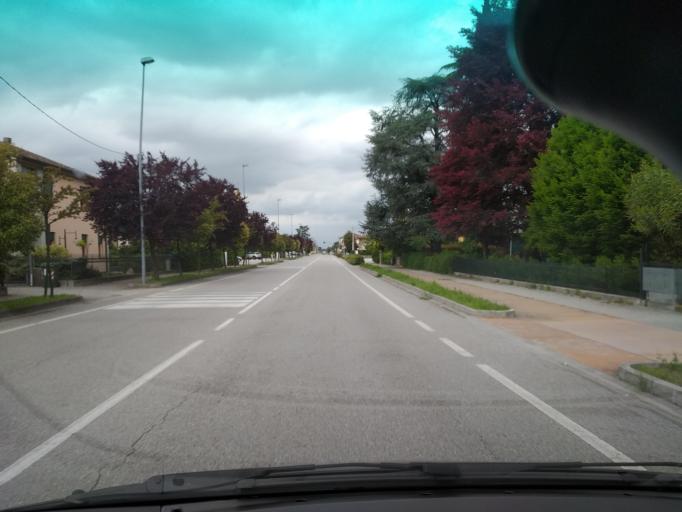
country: IT
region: Veneto
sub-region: Provincia di Padova
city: Tremignon
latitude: 45.5174
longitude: 11.8054
